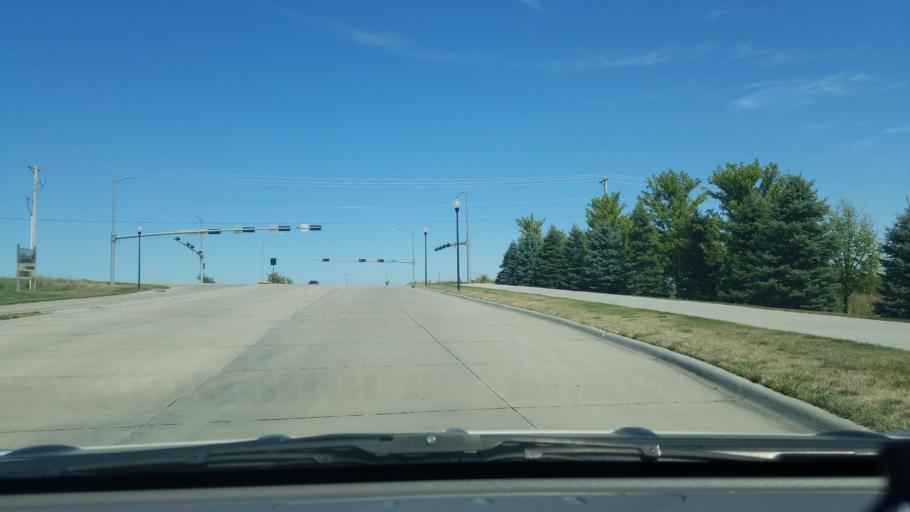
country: US
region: Nebraska
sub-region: Sarpy County
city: Papillion
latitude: 41.1468
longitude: -96.1010
